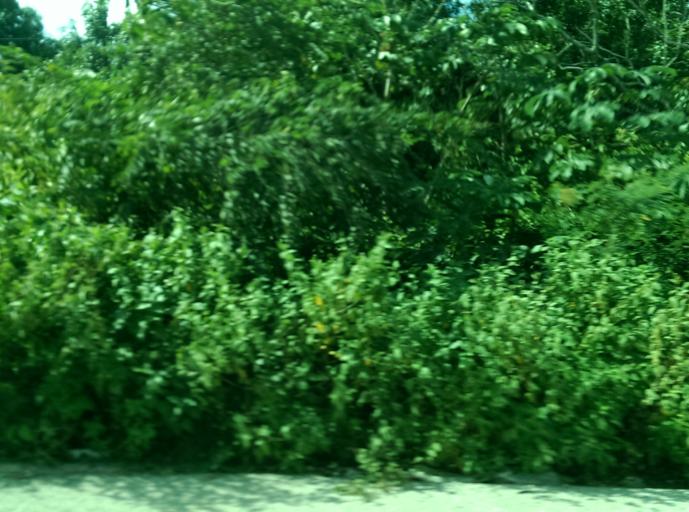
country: MX
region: Quintana Roo
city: Tulum
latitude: 20.2204
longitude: -87.4556
